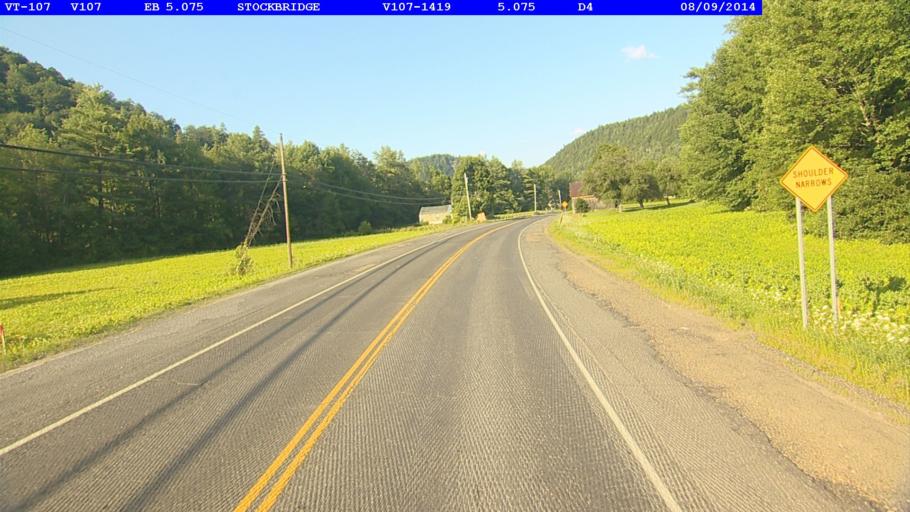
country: US
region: Vermont
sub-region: Orange County
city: Randolph
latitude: 43.7844
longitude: -72.6893
